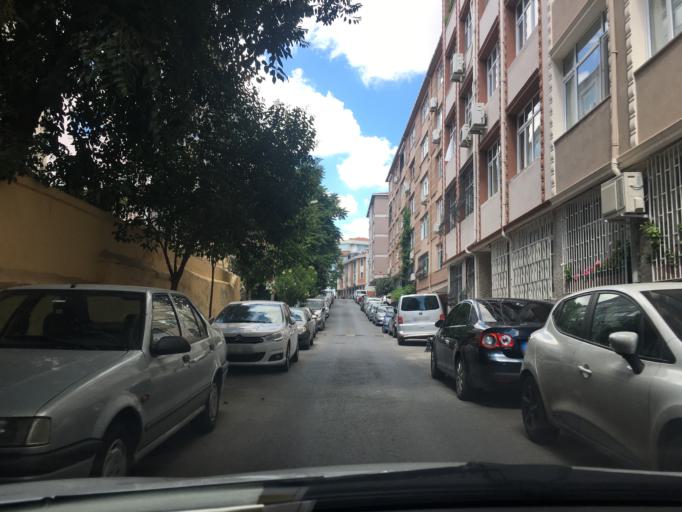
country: TR
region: Istanbul
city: Istanbul
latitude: 41.0117
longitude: 28.9365
